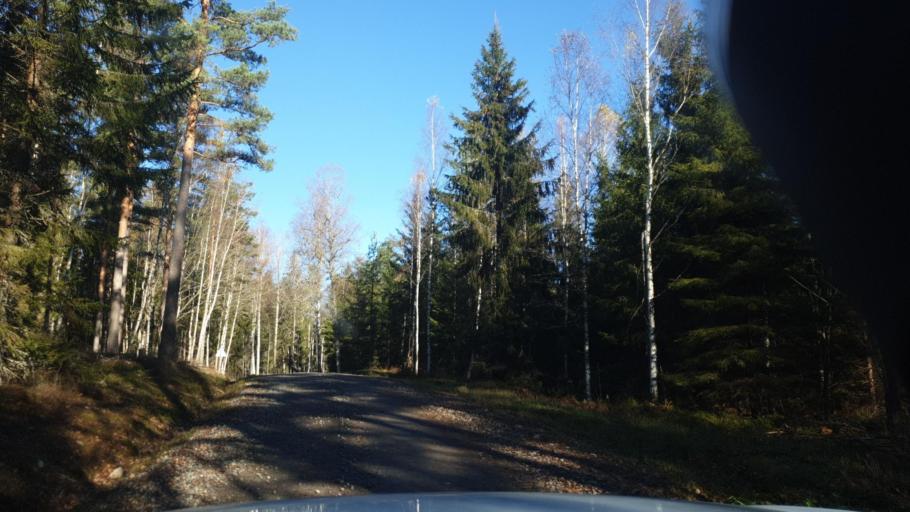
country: SE
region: Vaermland
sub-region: Karlstads Kommun
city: Valberg
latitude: 59.4524
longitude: 13.0942
